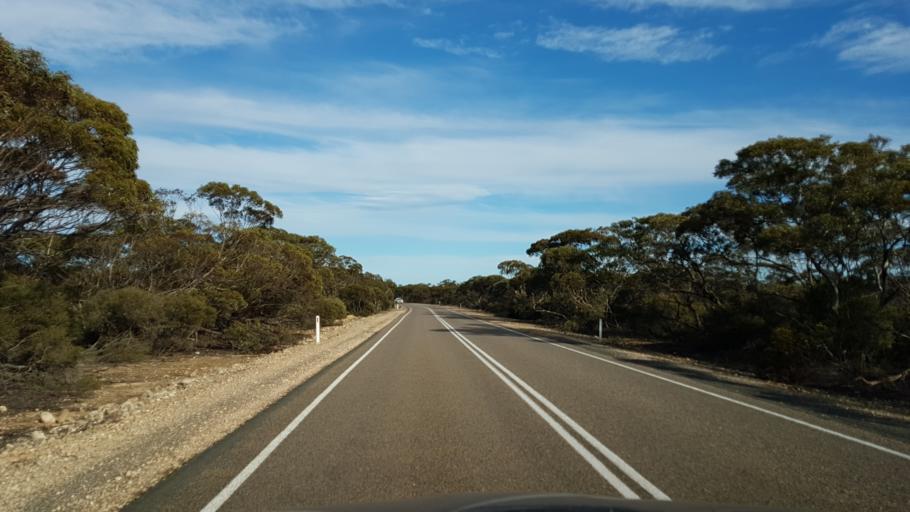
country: AU
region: South Australia
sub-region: Mid Murray
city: Mannum
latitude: -35.0076
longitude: 139.5282
